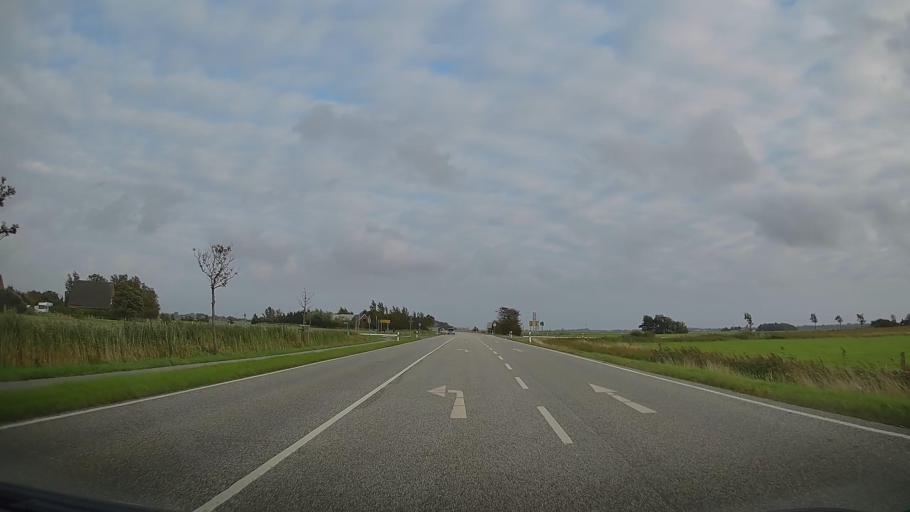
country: DE
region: Schleswig-Holstein
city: Sankt Peter-Ording
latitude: 54.3281
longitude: 8.6386
